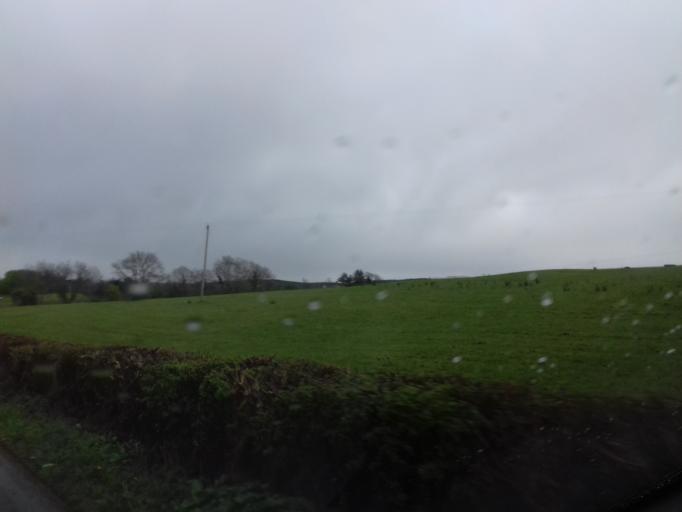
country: IE
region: Connaught
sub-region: County Leitrim
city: Manorhamilton
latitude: 54.2812
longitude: -7.9511
